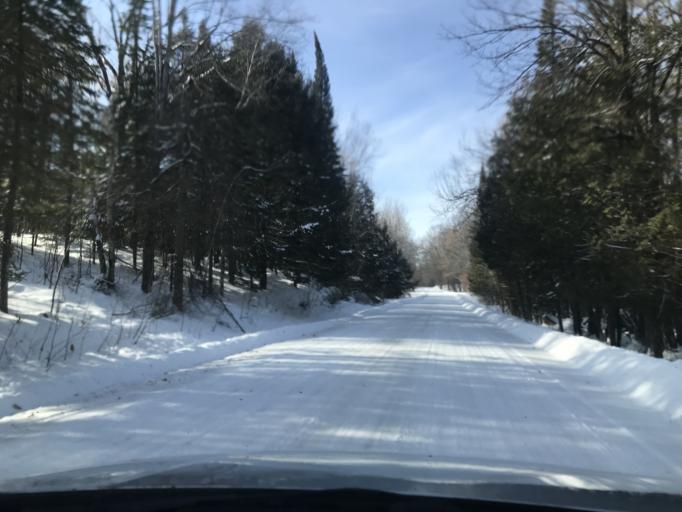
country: US
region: Wisconsin
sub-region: Oconto County
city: Gillett
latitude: 45.1459
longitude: -88.2311
